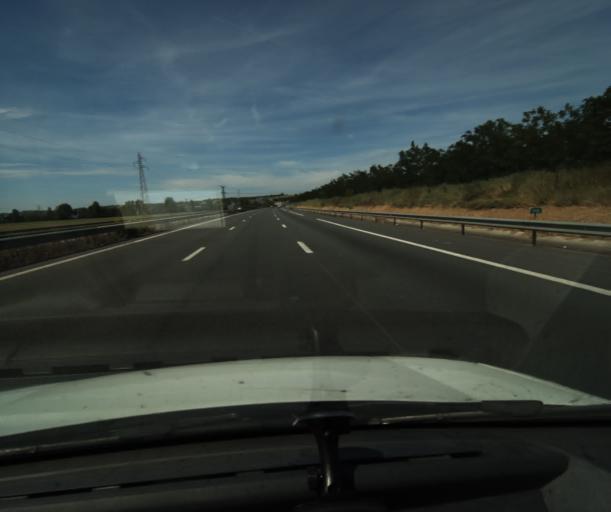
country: FR
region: Midi-Pyrenees
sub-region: Departement de la Haute-Garonne
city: Saint-Sauveur
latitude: 43.7554
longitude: 1.3858
